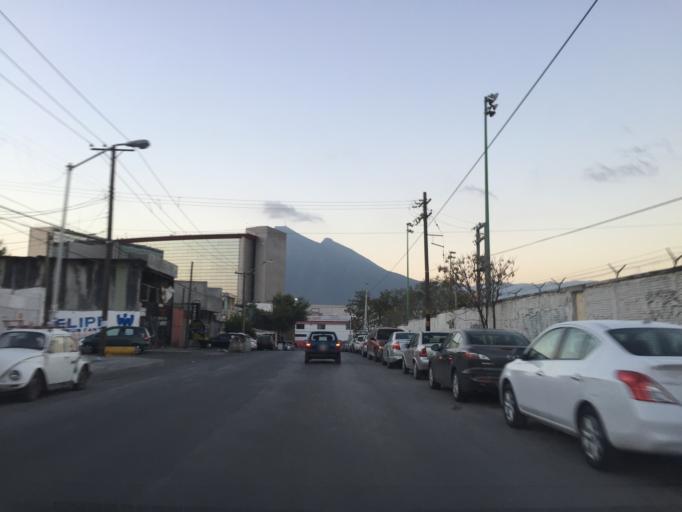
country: MX
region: Nuevo Leon
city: Guadalupe
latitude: 25.6964
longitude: -100.2237
